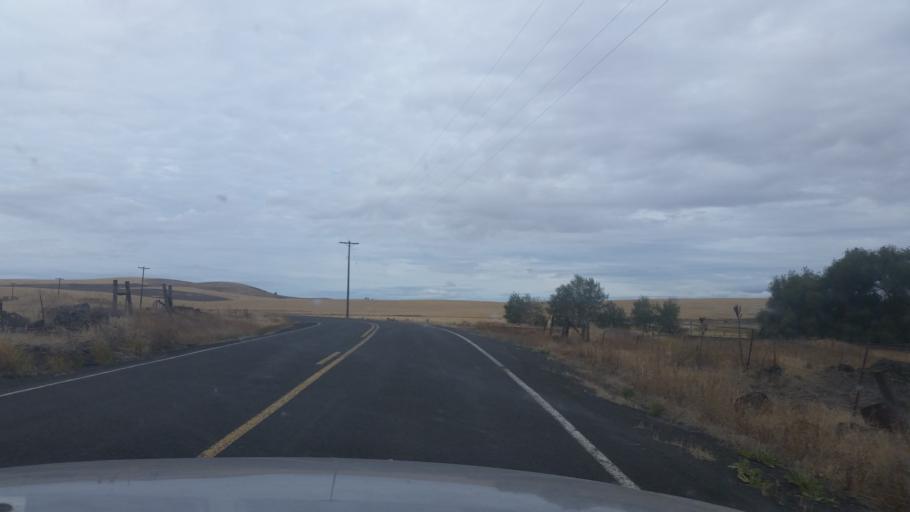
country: US
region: Washington
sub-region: Spokane County
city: Medical Lake
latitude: 47.5206
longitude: -117.9018
